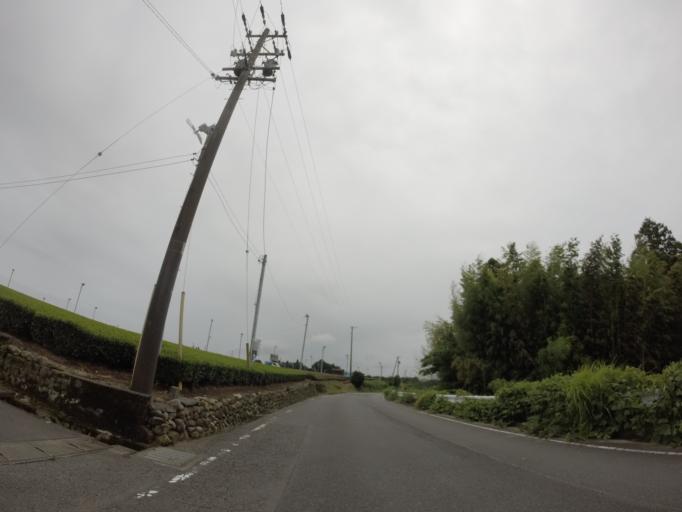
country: JP
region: Shizuoka
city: Kanaya
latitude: 34.8012
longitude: 138.1406
